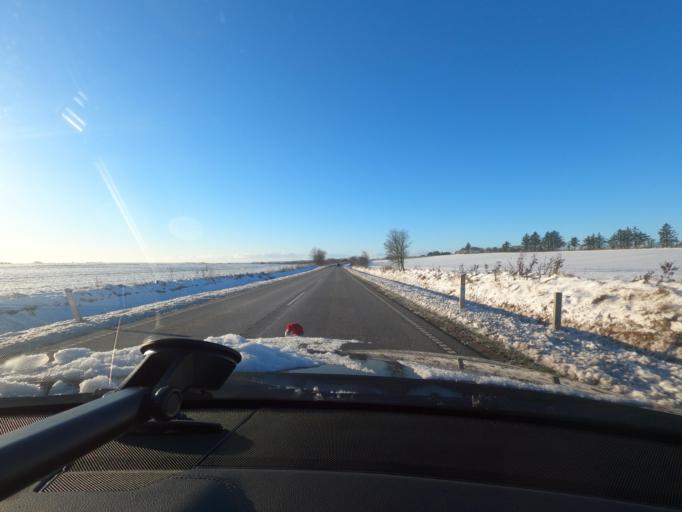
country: DK
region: South Denmark
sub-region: Tonder Kommune
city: Toftlund
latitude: 55.1793
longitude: 9.0584
